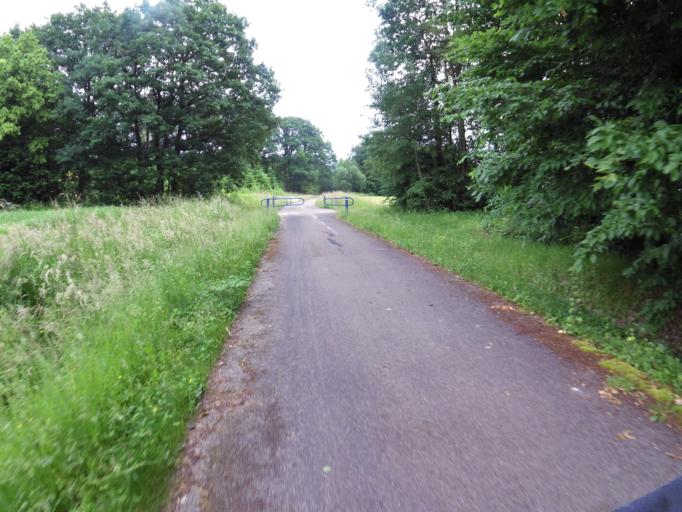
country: FR
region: Champagne-Ardenne
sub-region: Departement de la Haute-Marne
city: Montier-en-Der
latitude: 48.5449
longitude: 4.8095
